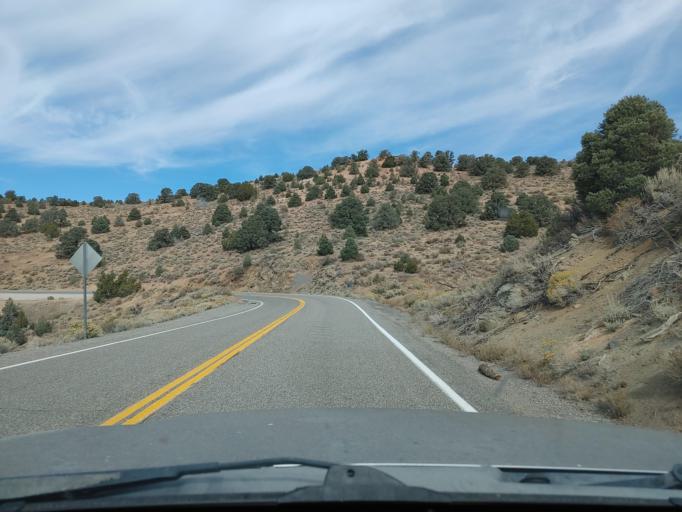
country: US
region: Nevada
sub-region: Storey County
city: Virginia City
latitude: 39.2966
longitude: -119.6445
